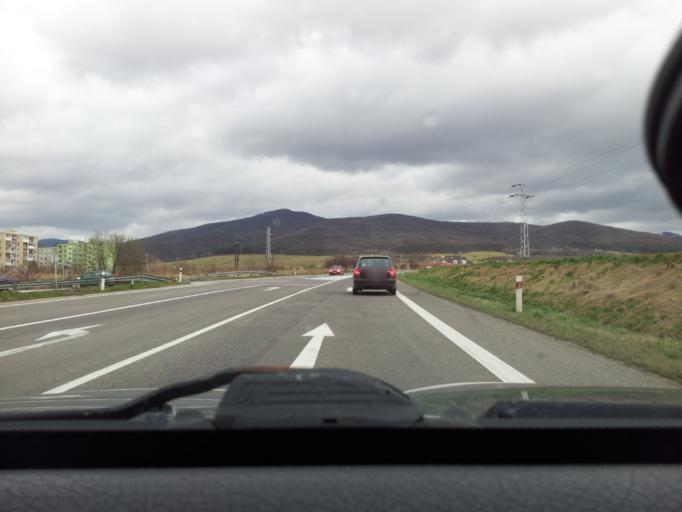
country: SK
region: Kosicky
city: Roznava
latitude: 48.6477
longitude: 20.5397
